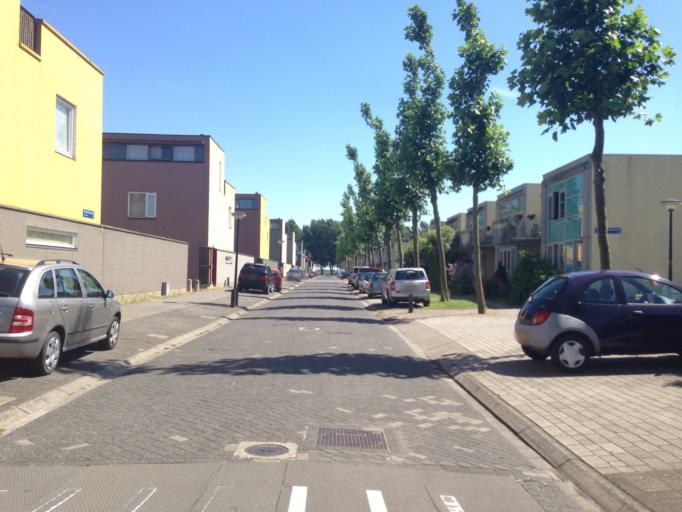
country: NL
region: Flevoland
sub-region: Gemeente Almere
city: Almere Stad
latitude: 52.3921
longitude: 5.2955
